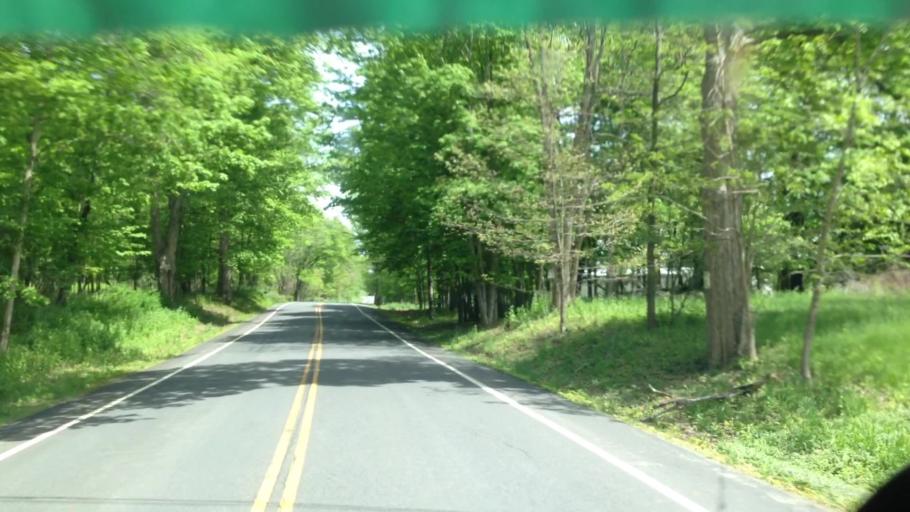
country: US
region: New York
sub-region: Dutchess County
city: Pine Plains
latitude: 42.0605
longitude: -73.6226
